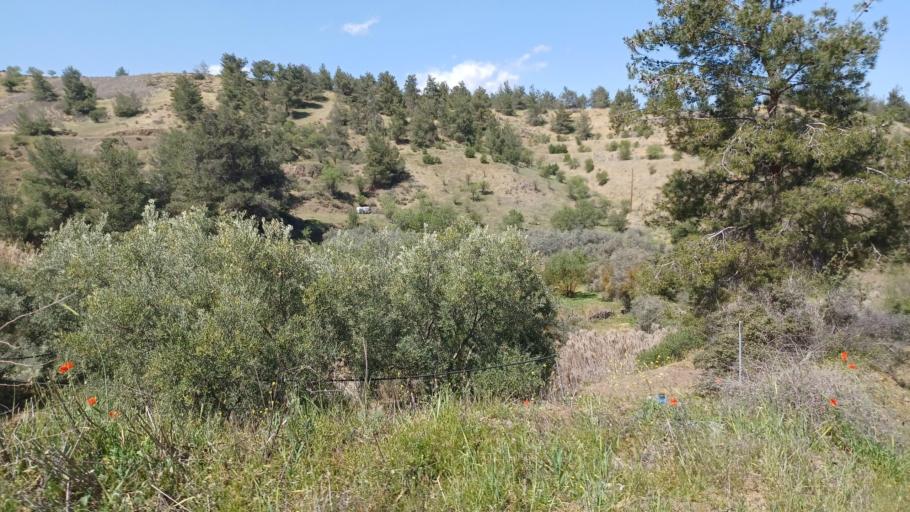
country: CY
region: Lefkosia
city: Astromeritis
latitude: 35.0618
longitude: 33.0219
